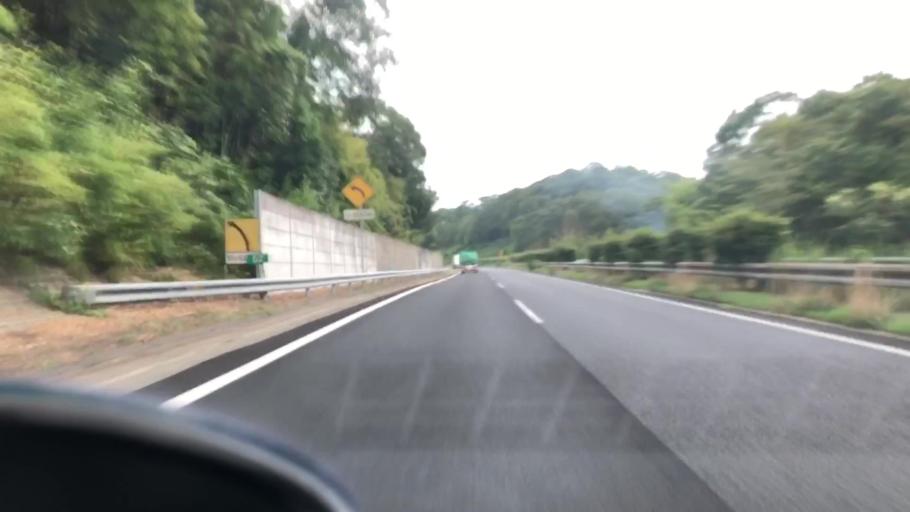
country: JP
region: Hyogo
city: Yashiro
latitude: 34.9126
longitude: 135.0404
